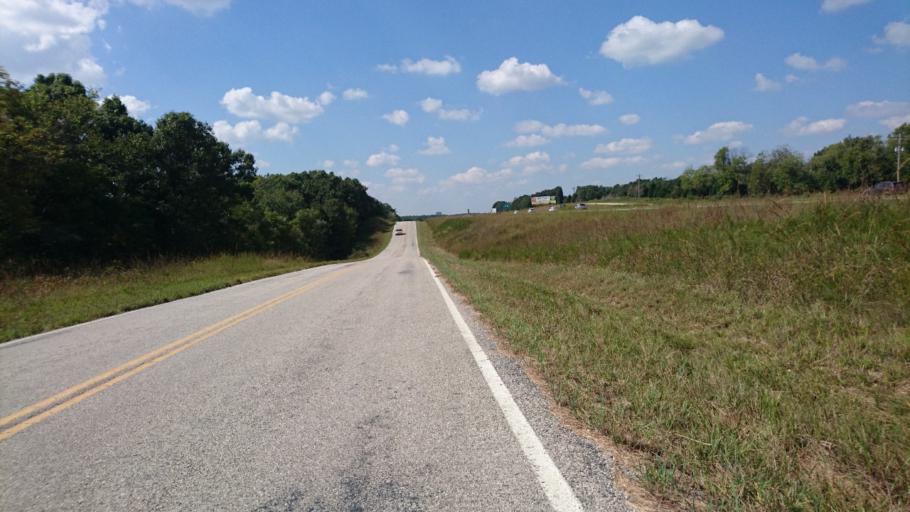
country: US
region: Missouri
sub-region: Pulaski County
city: Richland
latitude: 37.7556
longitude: -92.4807
